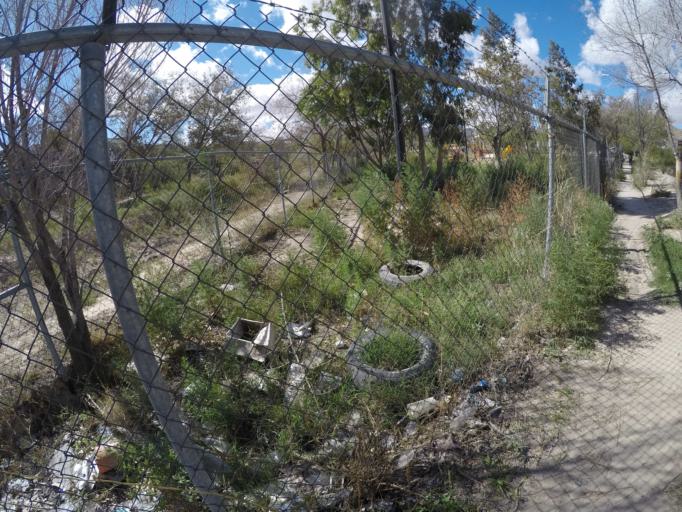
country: MX
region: Chihuahua
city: Ciudad Juarez
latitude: 31.6905
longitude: -106.4861
